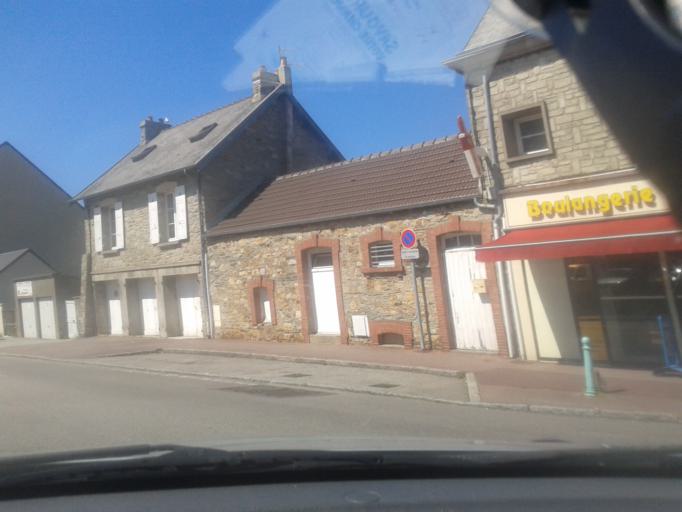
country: FR
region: Lower Normandy
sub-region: Departement de la Manche
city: Octeville
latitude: 49.6291
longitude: -1.6411
